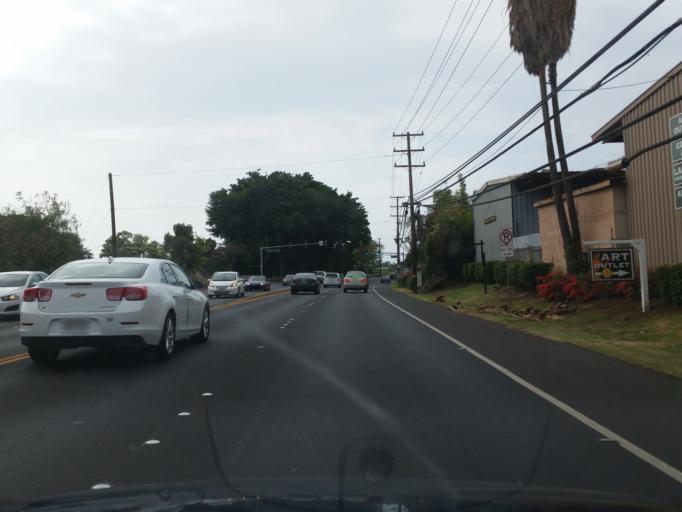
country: US
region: Hawaii
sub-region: Maui County
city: Lahaina
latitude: 20.8807
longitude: -156.6801
